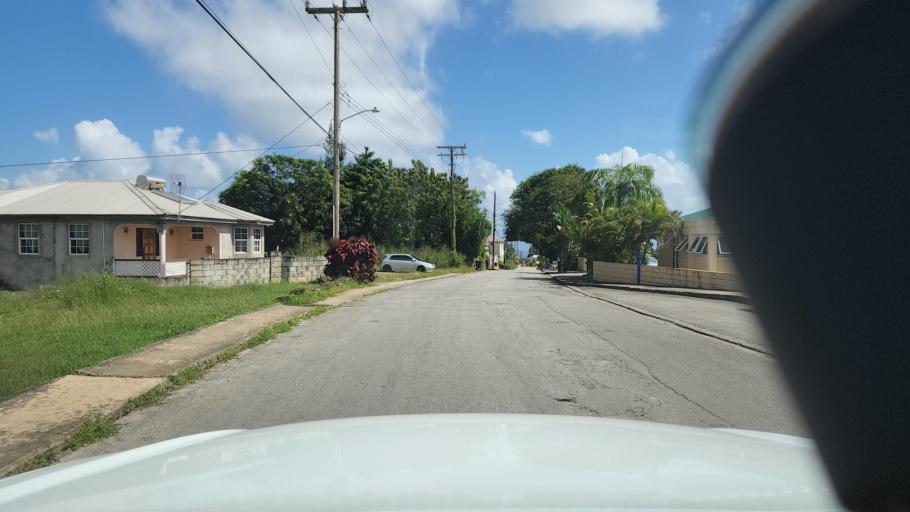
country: BB
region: Saint John
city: Four Cross Roads
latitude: 13.1822
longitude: -59.4965
